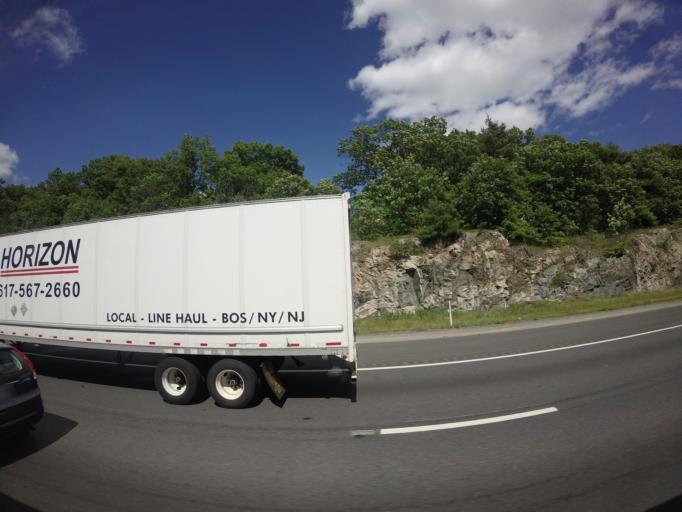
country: US
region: Massachusetts
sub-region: Middlesex County
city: Wilmington
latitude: 42.5666
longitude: -71.1451
